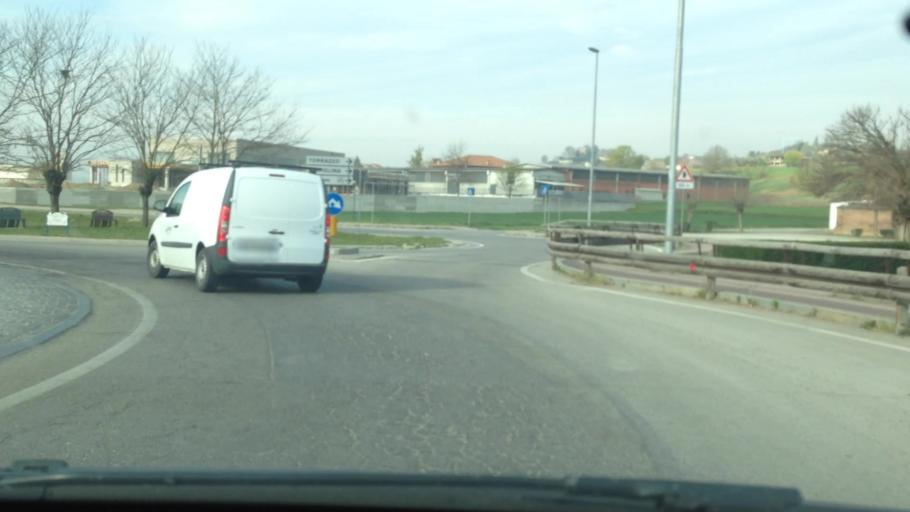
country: IT
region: Piedmont
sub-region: Provincia di Asti
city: San Damiano d'Asti
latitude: 44.8261
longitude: 8.0587
